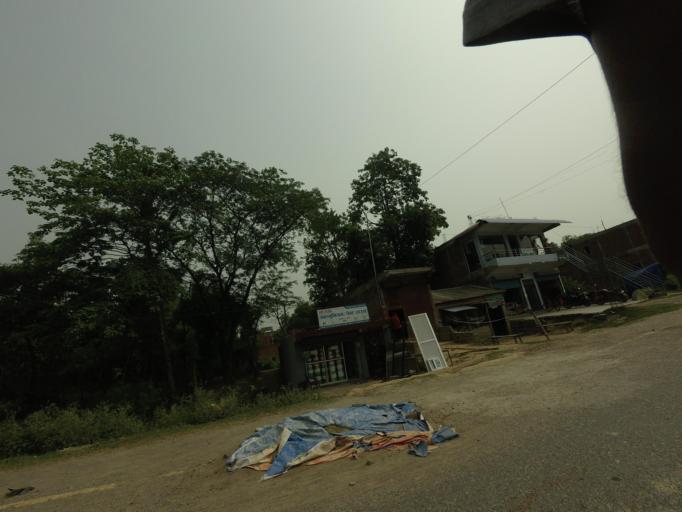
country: NP
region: Western Region
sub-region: Lumbini Zone
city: Bhairahawa
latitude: 27.5059
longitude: 83.3632
